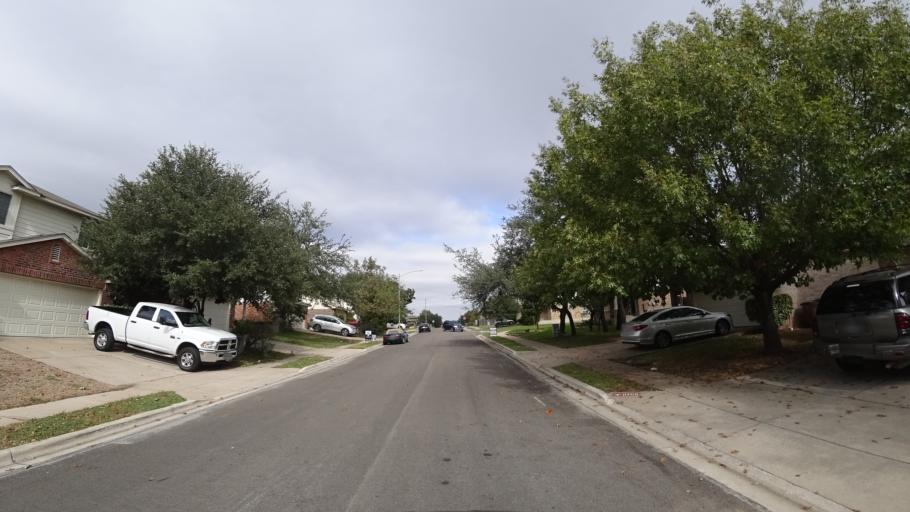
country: US
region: Texas
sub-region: Travis County
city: Manchaca
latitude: 30.1528
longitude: -97.8446
